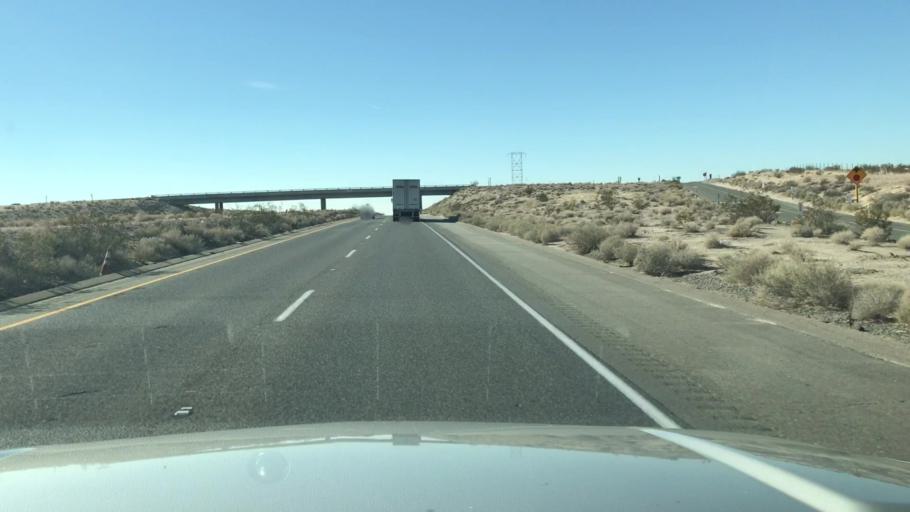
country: US
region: California
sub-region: San Bernardino County
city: Fort Irwin
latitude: 35.0120
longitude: -116.5291
